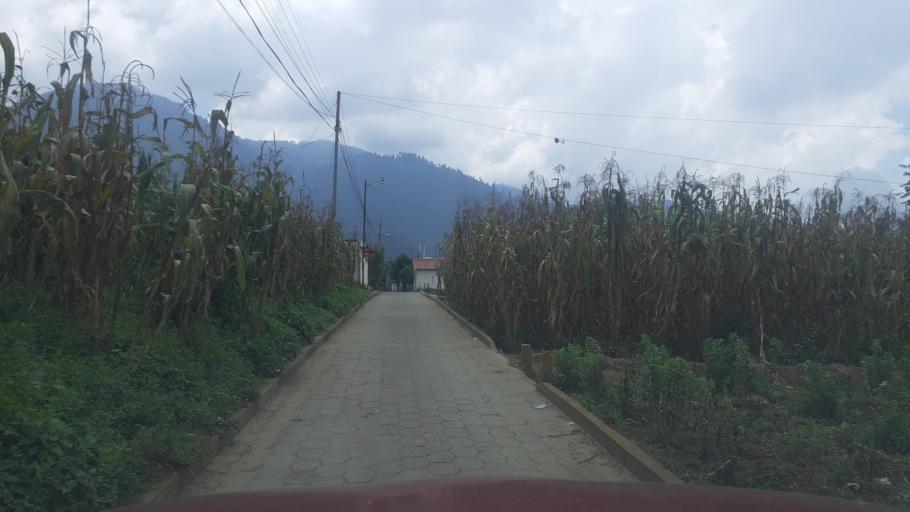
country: GT
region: Quetzaltenango
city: Cantel
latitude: 14.8170
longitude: -91.4508
